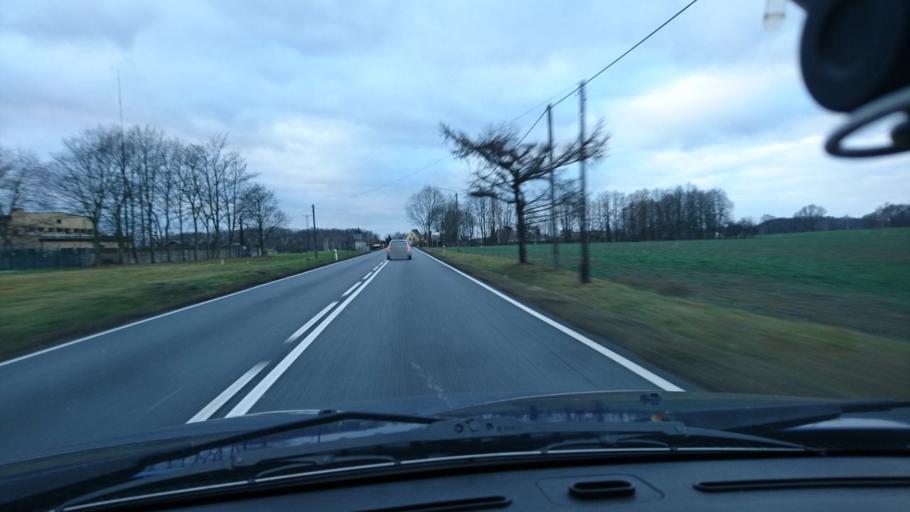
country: PL
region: Lodz Voivodeship
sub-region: Powiat wieruszowski
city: Boleslawiec
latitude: 51.1618
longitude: 18.1575
